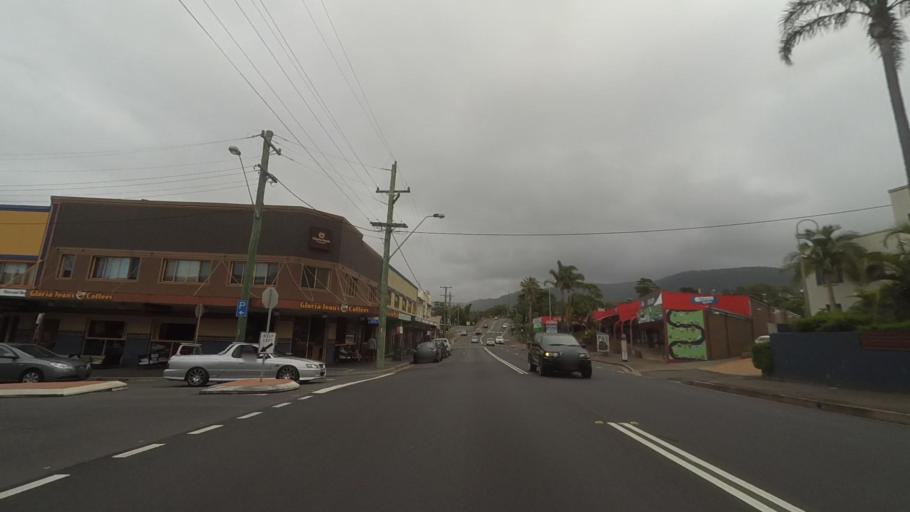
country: AU
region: New South Wales
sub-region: Wollongong
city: Bulli
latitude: -34.3153
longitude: 150.9228
